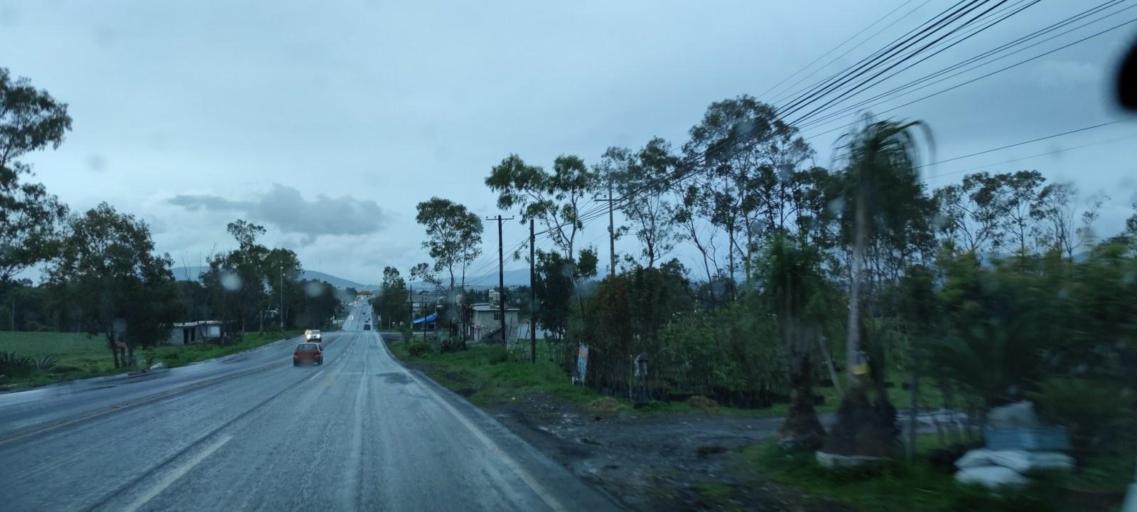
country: MX
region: Mexico
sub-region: Jilotepec
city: Doxhicho
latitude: 19.9436
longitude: -99.5592
